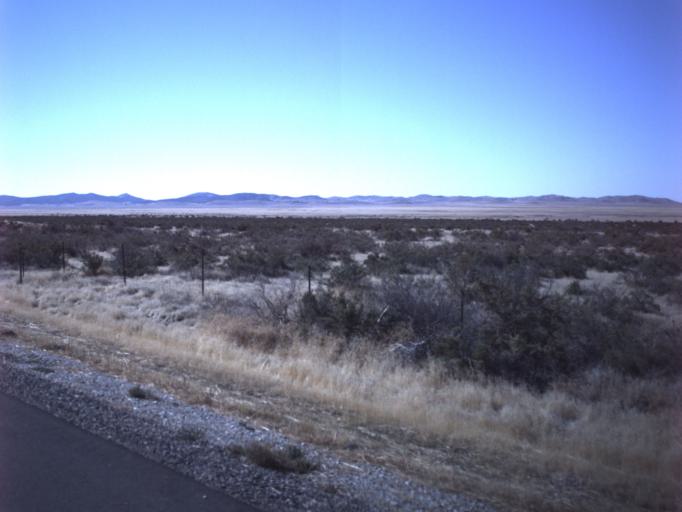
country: US
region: Utah
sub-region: Tooele County
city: Grantsville
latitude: 40.3569
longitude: -112.7457
